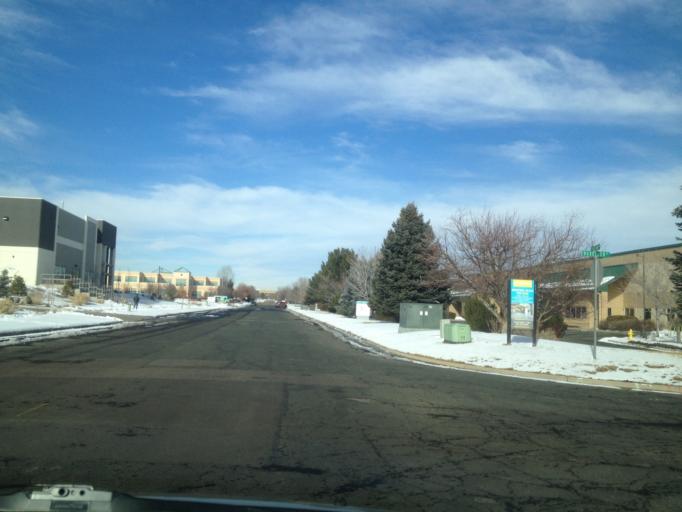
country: US
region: Colorado
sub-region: Boulder County
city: Louisville
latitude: 39.9627
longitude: -105.1197
